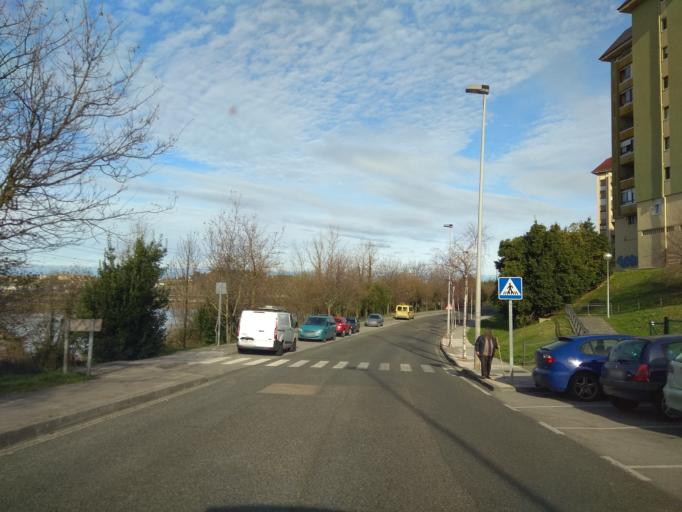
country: ES
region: Cantabria
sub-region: Provincia de Cantabria
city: El Astillero
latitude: 43.4019
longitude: -3.8259
